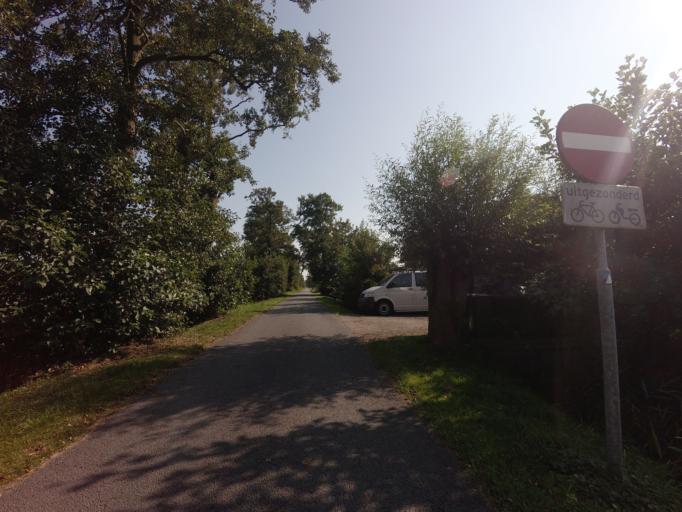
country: NL
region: Groningen
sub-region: Gemeente Zuidhorn
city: Zuidhorn
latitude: 53.2100
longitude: 6.4350
